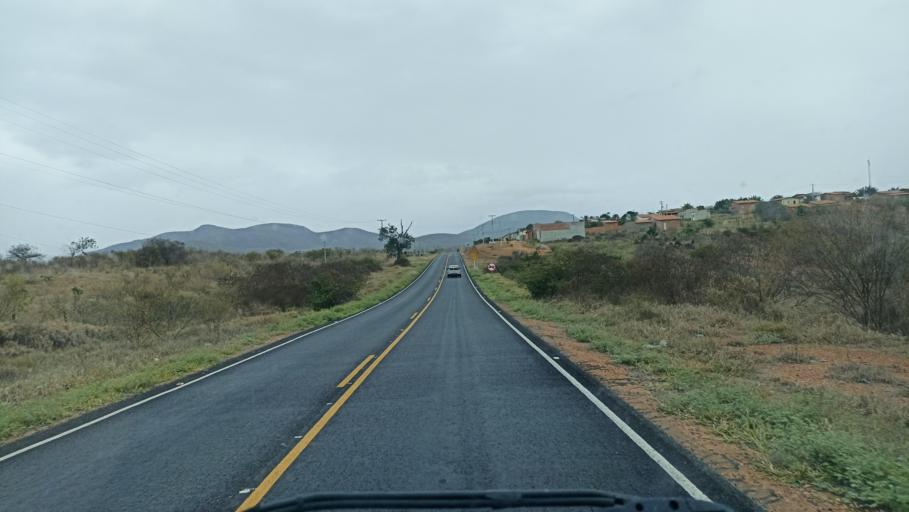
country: BR
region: Bahia
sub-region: Maracas
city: Maracas
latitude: -13.0482
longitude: -40.7416
